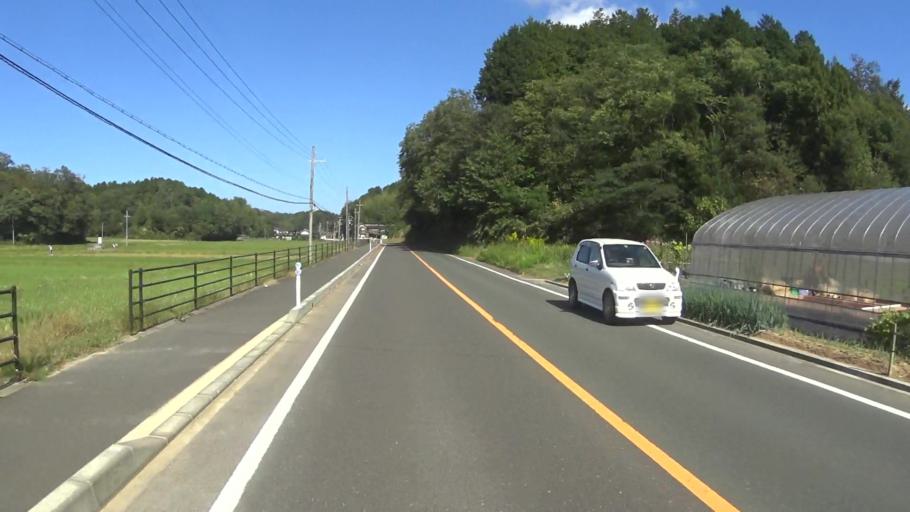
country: JP
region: Kyoto
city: Miyazu
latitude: 35.6493
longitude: 135.0687
